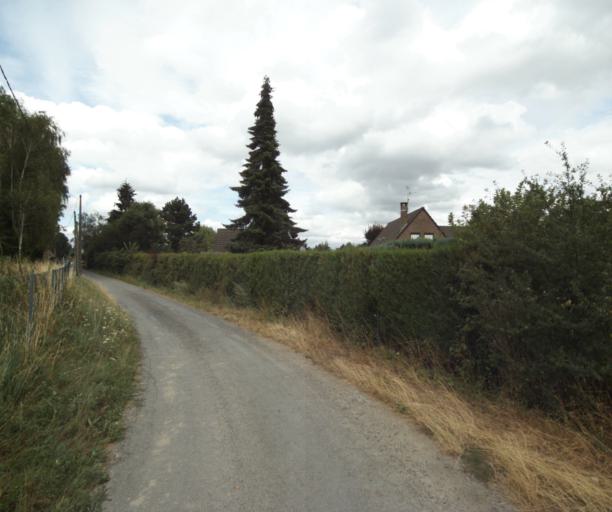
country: FR
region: Nord-Pas-de-Calais
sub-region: Departement du Nord
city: Bousbecque
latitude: 50.7611
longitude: 3.0897
